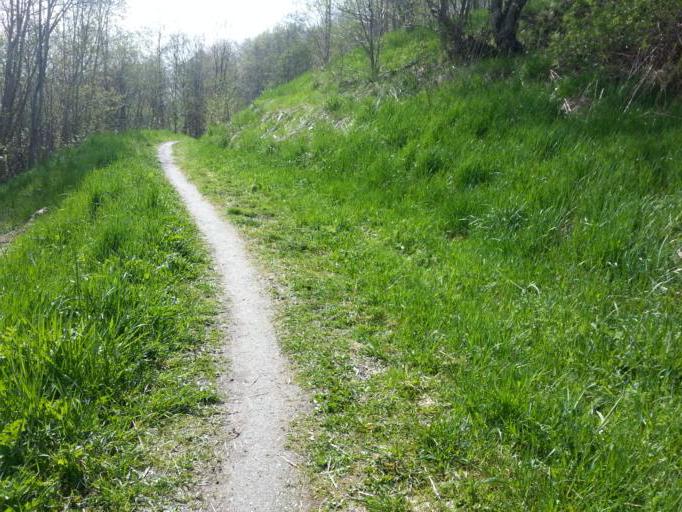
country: NO
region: Sor-Trondelag
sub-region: Trondheim
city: Trondheim
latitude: 63.3886
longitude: 10.3683
